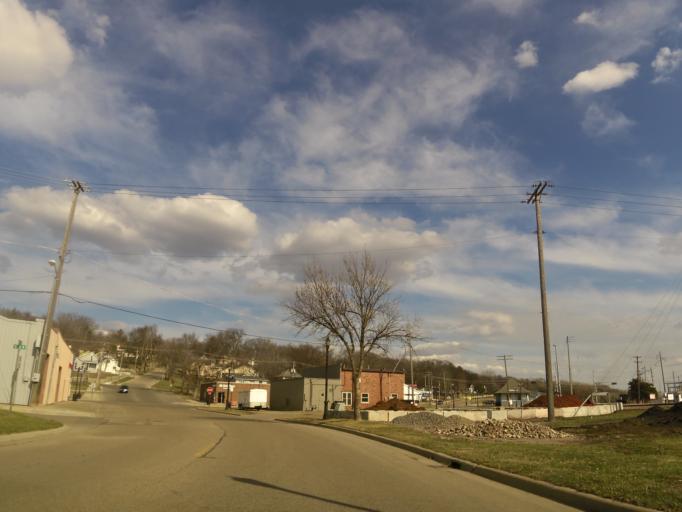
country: US
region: Minnesota
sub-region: Chippewa County
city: Montevideo
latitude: 44.9423
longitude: -95.7245
